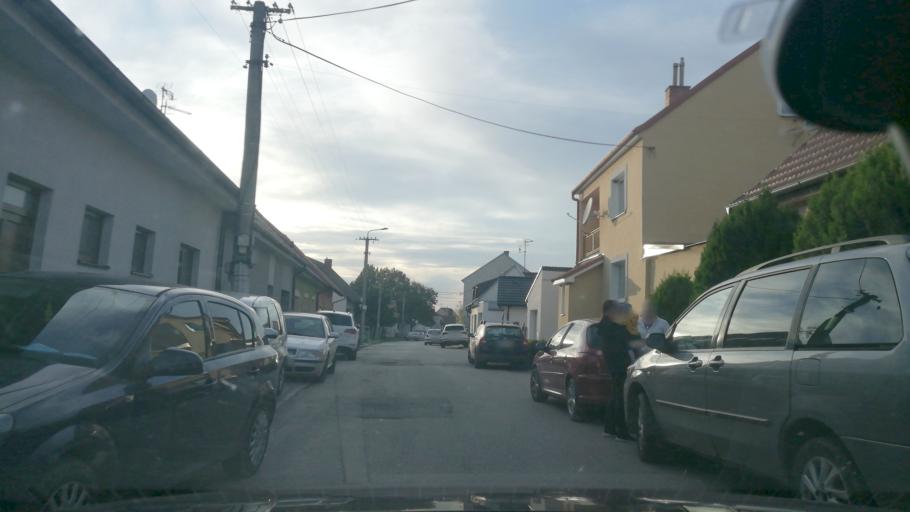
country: SK
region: Trnavsky
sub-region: Okres Skalica
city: Skalica
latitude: 48.8433
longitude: 17.2393
